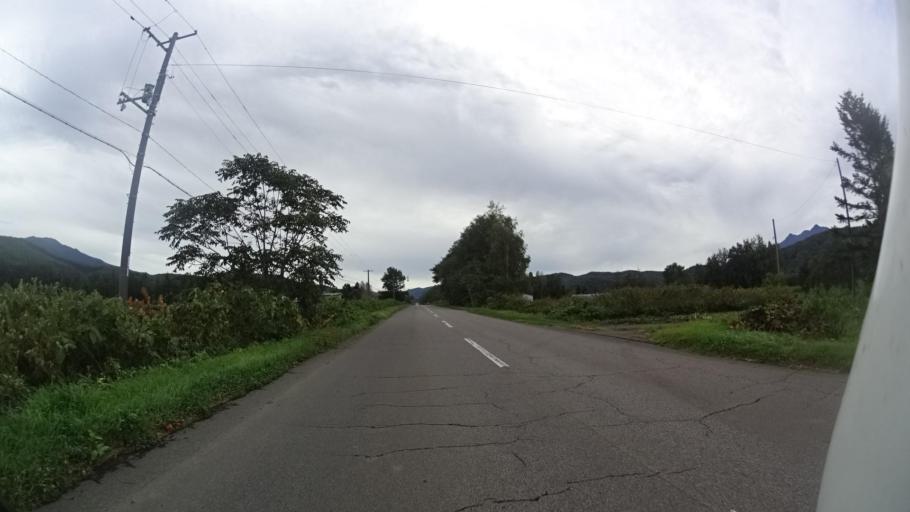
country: JP
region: Hokkaido
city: Shibetsu
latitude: 43.8649
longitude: 144.7550
